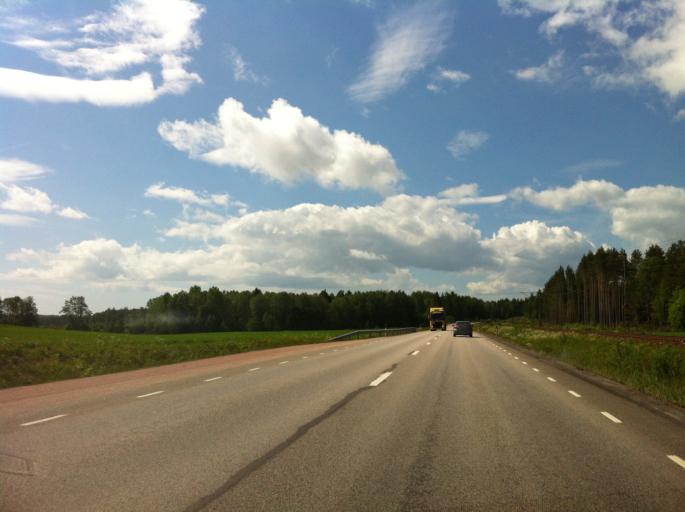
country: SE
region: Vaermland
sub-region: Saffle Kommun
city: Saeffle
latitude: 59.1605
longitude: 12.9920
